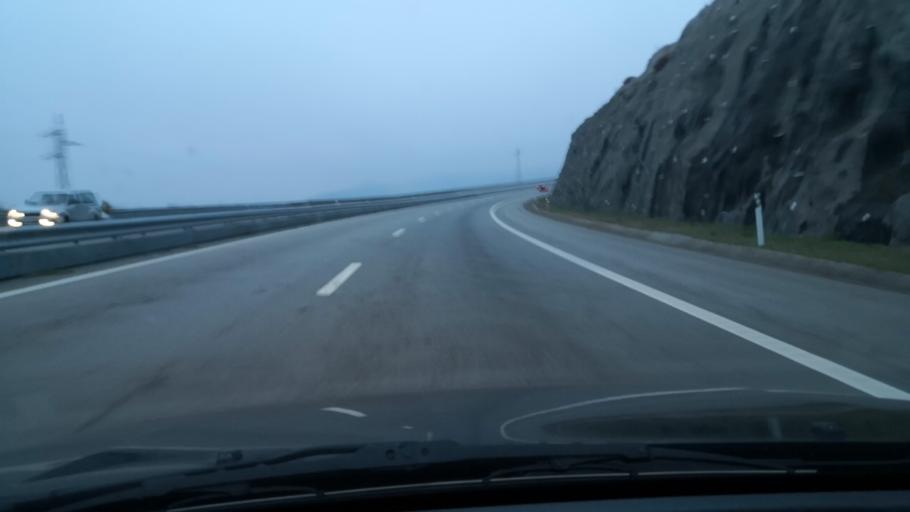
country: PT
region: Vila Real
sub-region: Santa Marta de Penaguiao
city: Santa Marta de Penaguiao
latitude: 41.2254
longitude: -7.7355
